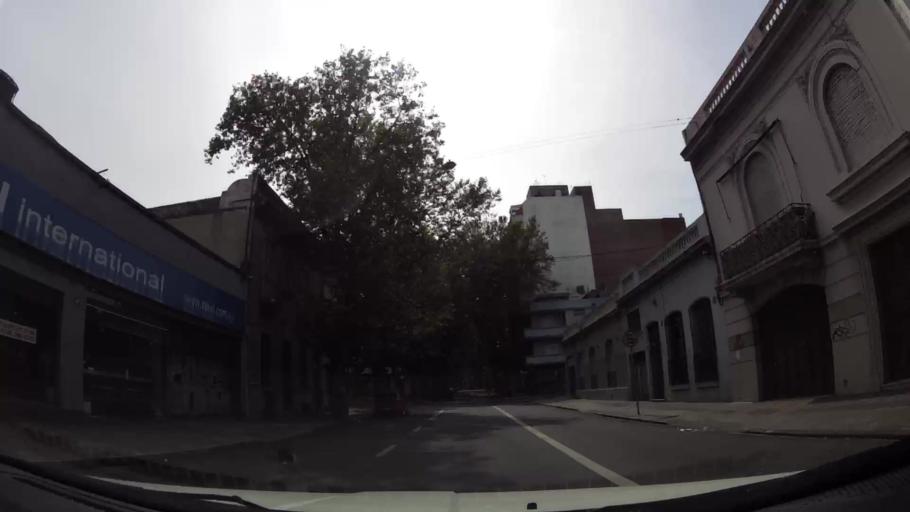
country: UY
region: Montevideo
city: Montevideo
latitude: -34.9035
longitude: -56.1719
